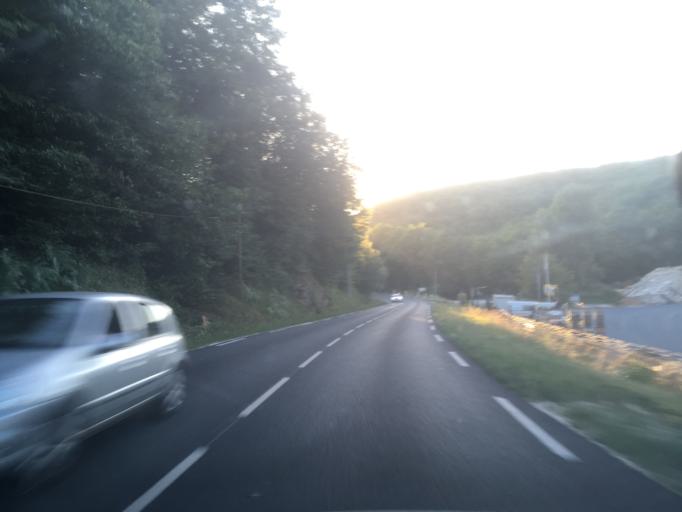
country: FR
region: Aquitaine
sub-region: Departement de la Dordogne
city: Sarlat-la-Caneda
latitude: 44.8524
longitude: 1.1977
